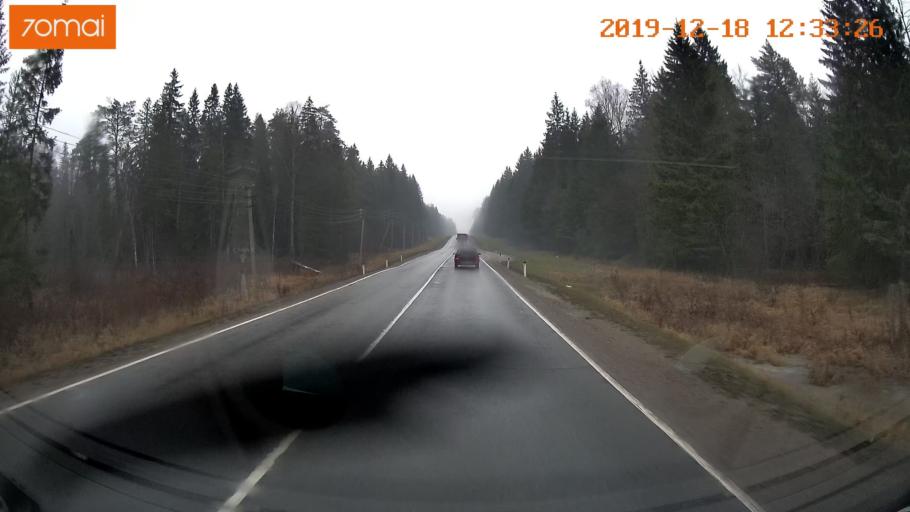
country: RU
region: Moskovskaya
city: Rumyantsevo
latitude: 56.1128
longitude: 36.5608
